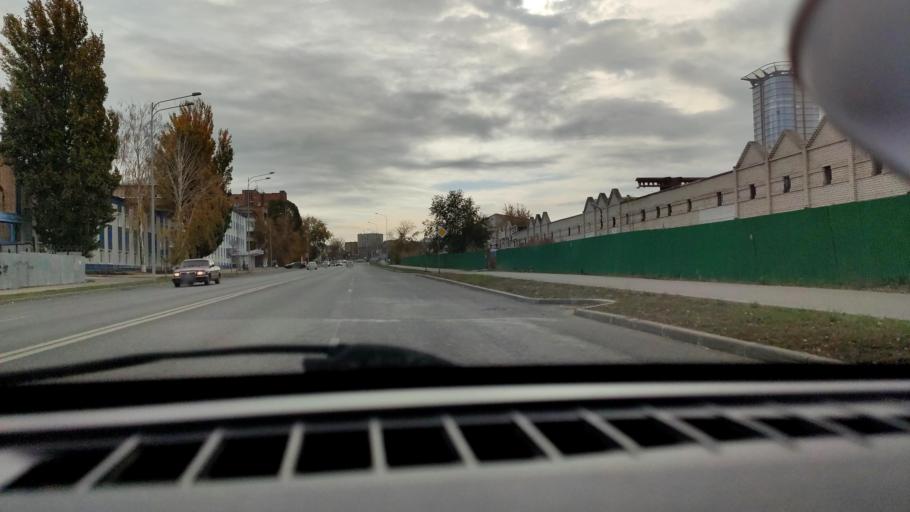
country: RU
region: Samara
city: Samara
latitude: 53.2065
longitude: 50.1550
